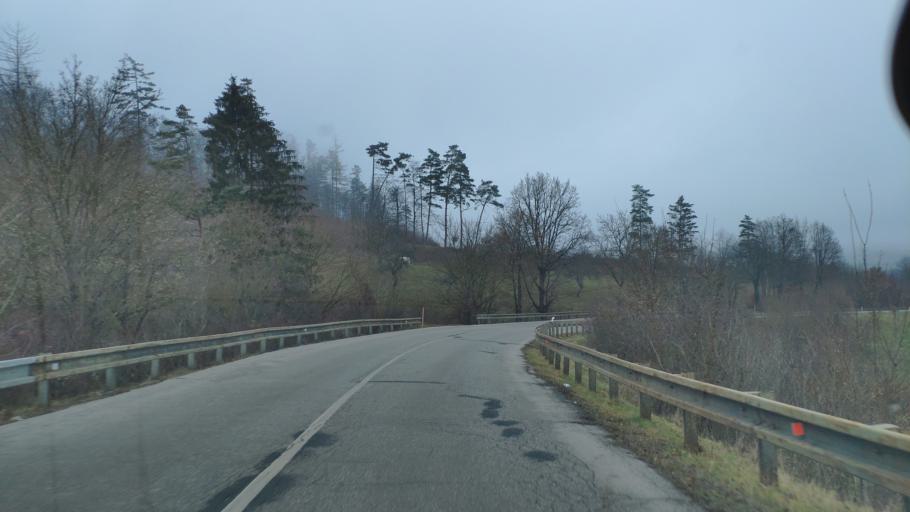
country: SK
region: Kosicky
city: Dobsina
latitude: 48.6456
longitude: 20.3608
